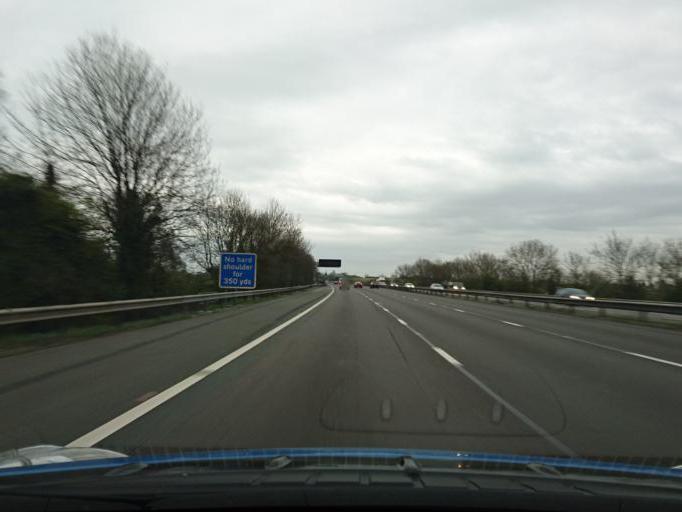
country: GB
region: England
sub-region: Staffordshire
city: Stone
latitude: 52.8957
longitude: -2.1820
